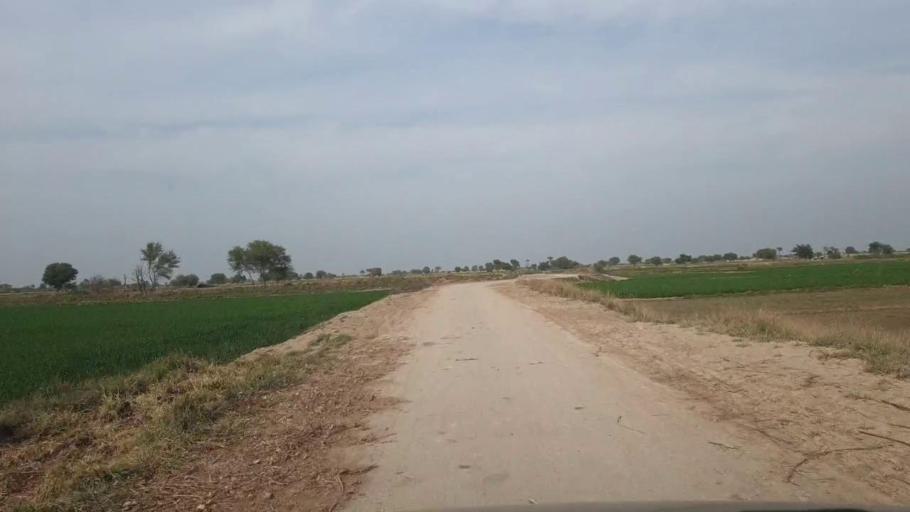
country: PK
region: Sindh
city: Shahpur Chakar
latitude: 26.1125
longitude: 68.5049
